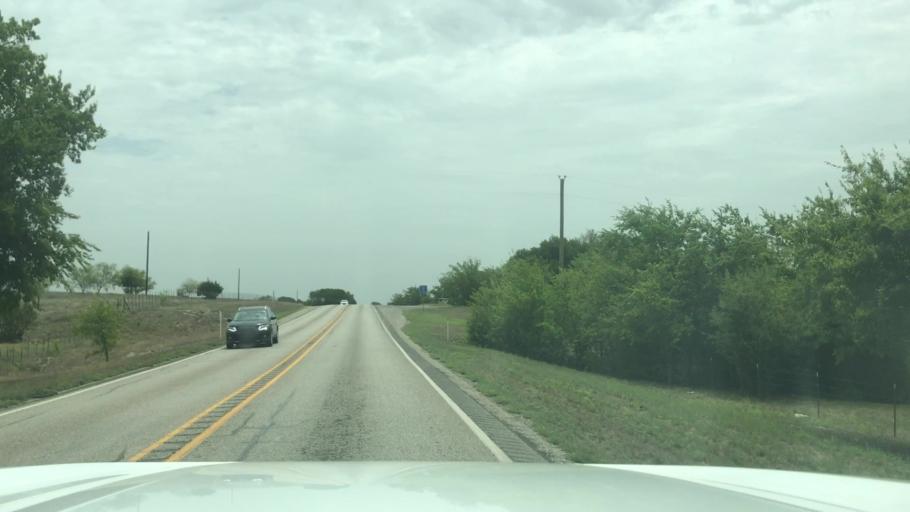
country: US
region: Texas
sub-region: Hamilton County
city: Hico
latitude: 32.0472
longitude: -98.1501
